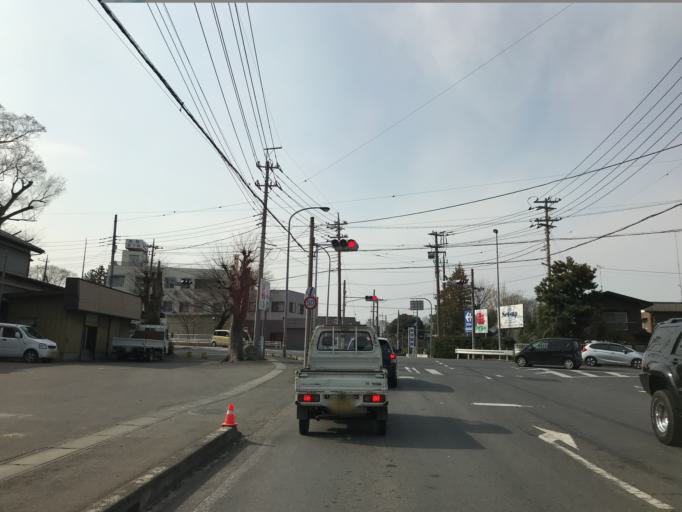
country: JP
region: Ibaraki
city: Okunoya
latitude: 36.2386
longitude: 140.3575
